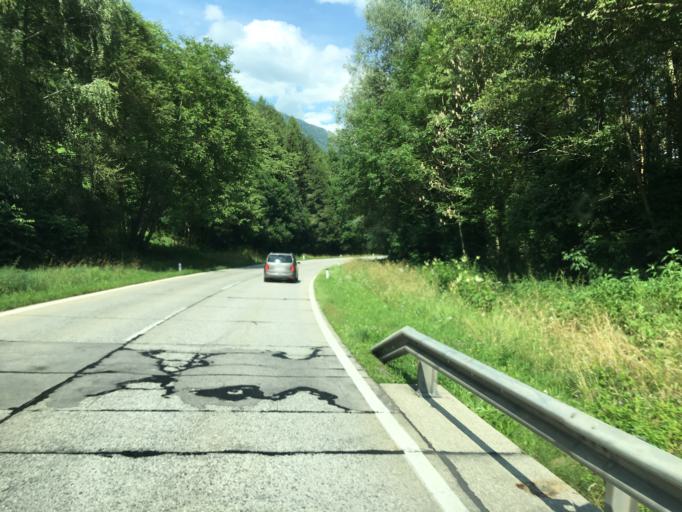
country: AT
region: Carinthia
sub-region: Politischer Bezirk Spittal an der Drau
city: Flattach
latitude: 46.9338
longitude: 13.0886
